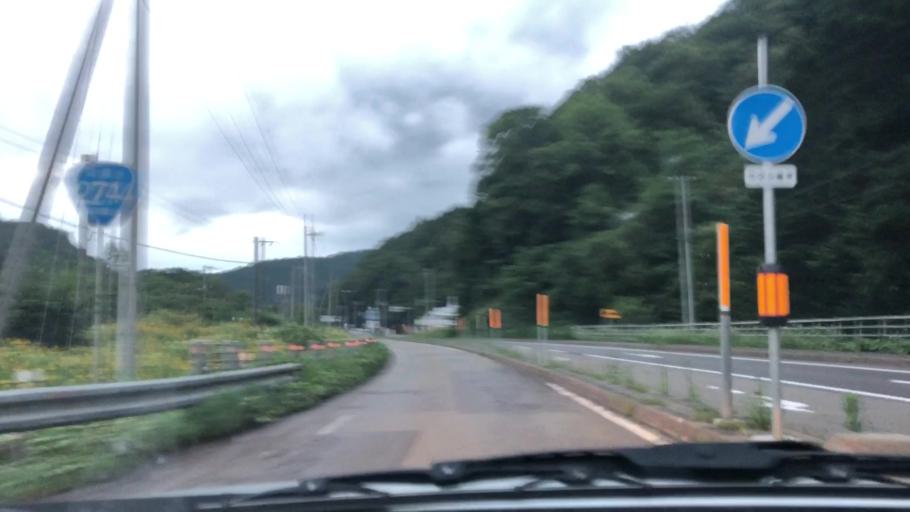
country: JP
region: Hokkaido
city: Chitose
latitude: 42.9125
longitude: 141.9717
